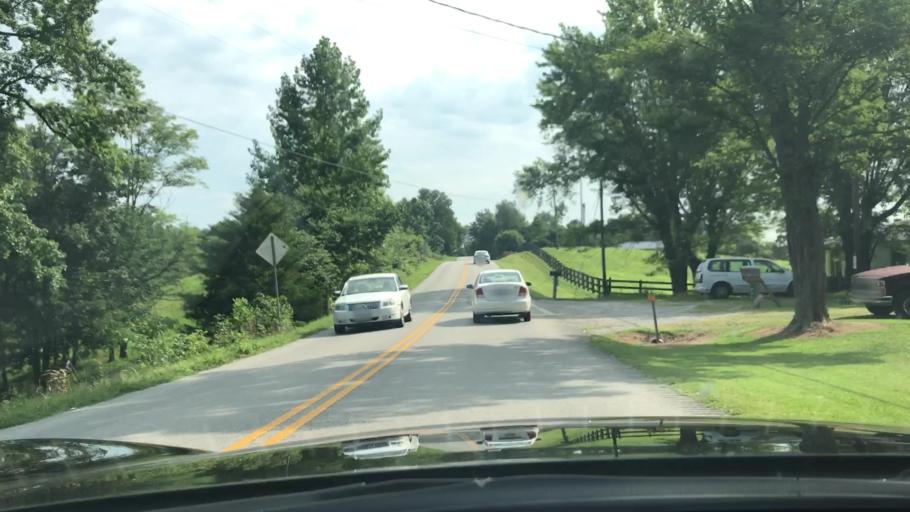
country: US
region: Kentucky
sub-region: Green County
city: Greensburg
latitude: 37.2746
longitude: -85.5259
